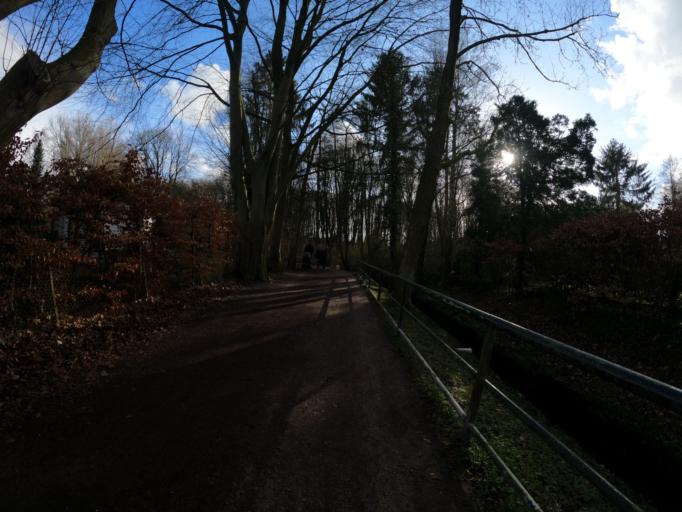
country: DE
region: Hamburg
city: Stellingen
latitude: 53.6265
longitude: 9.9347
